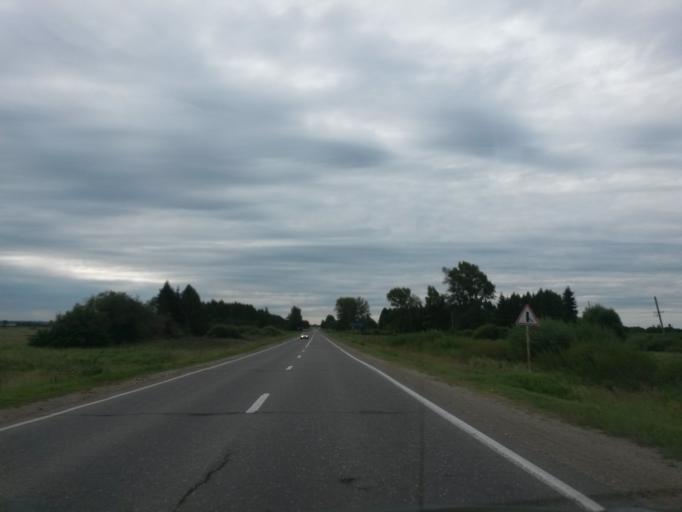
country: RU
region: Jaroslavl
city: Gavrilov-Yam
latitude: 57.3449
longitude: 39.7941
